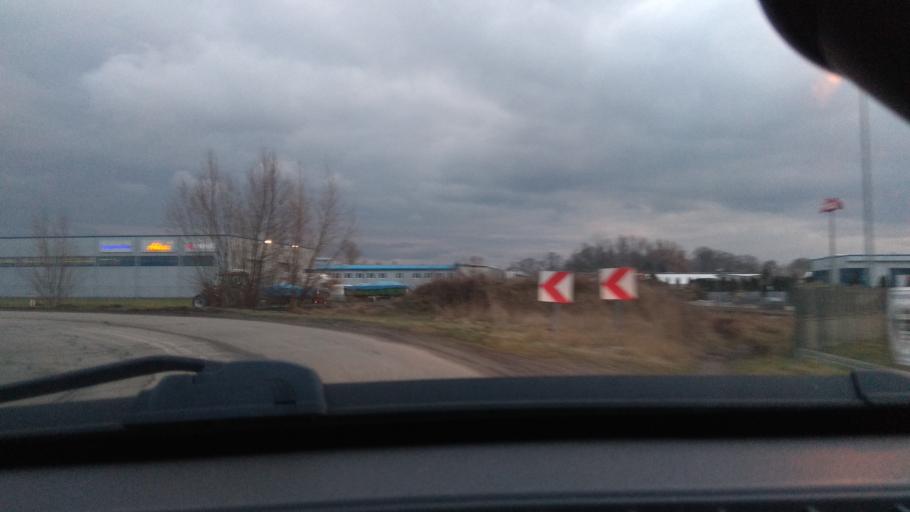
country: PL
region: Greater Poland Voivodeship
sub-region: Powiat kepinski
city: Kepno
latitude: 51.2888
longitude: 18.0061
